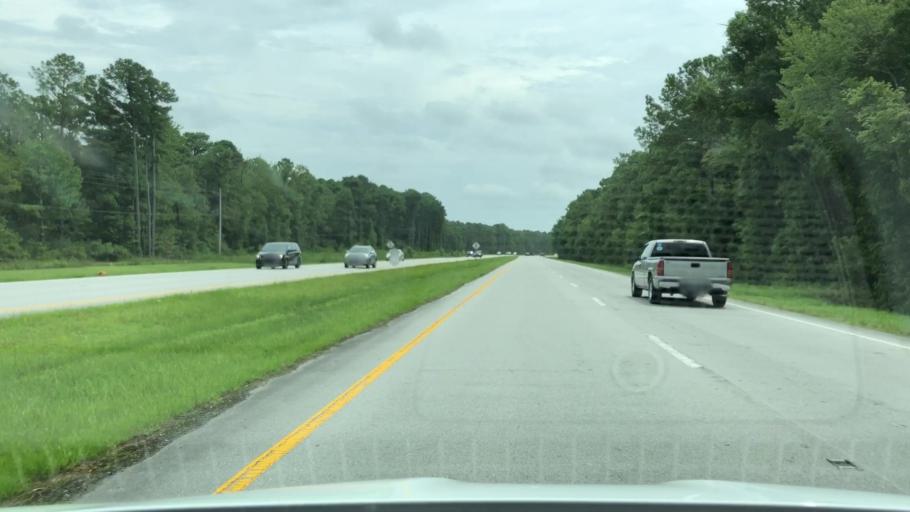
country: US
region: North Carolina
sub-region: Craven County
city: Havelock
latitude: 34.8535
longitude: -76.8922
